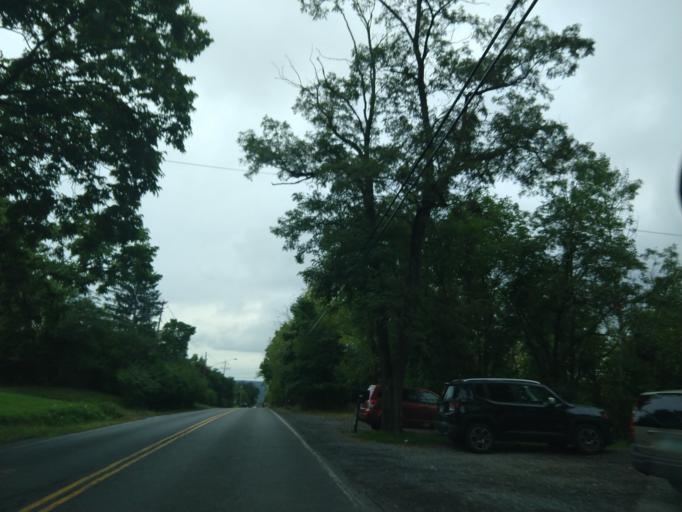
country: US
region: New York
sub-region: Tompkins County
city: South Hill
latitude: 42.4277
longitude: -76.4898
